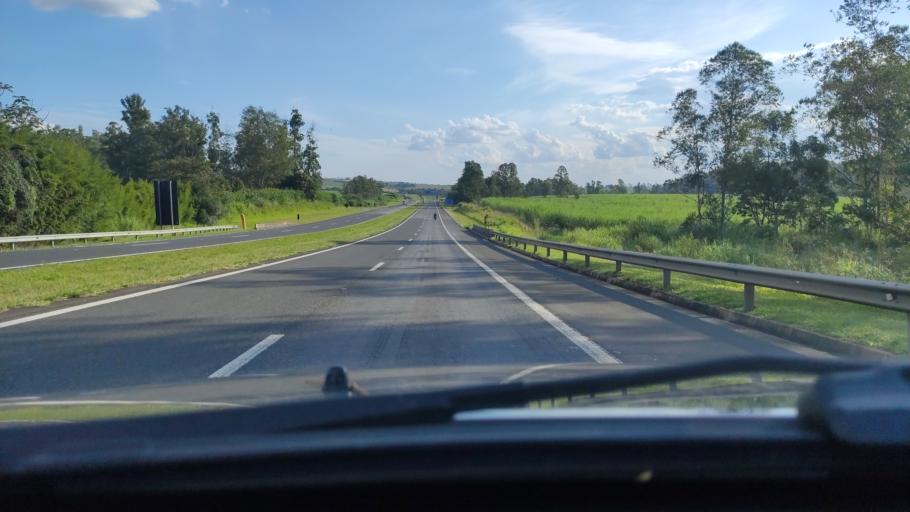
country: BR
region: Sao Paulo
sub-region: Itapira
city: Itapira
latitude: -22.4505
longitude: -46.8894
